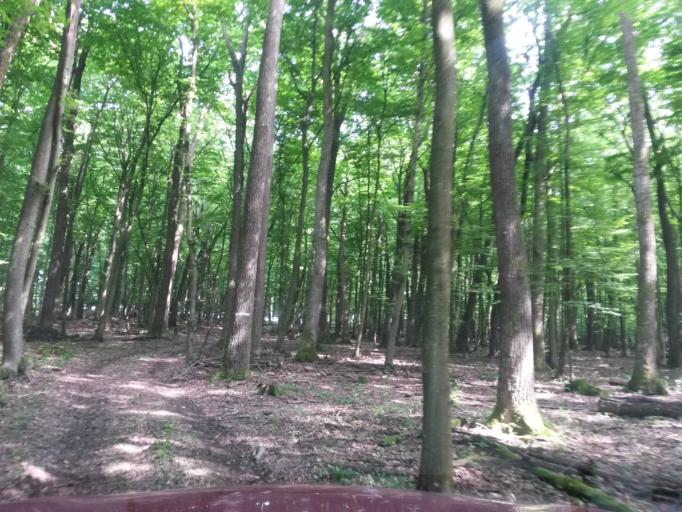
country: SK
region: Kosicky
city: Moldava nad Bodvou
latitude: 48.6385
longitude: 21.1016
